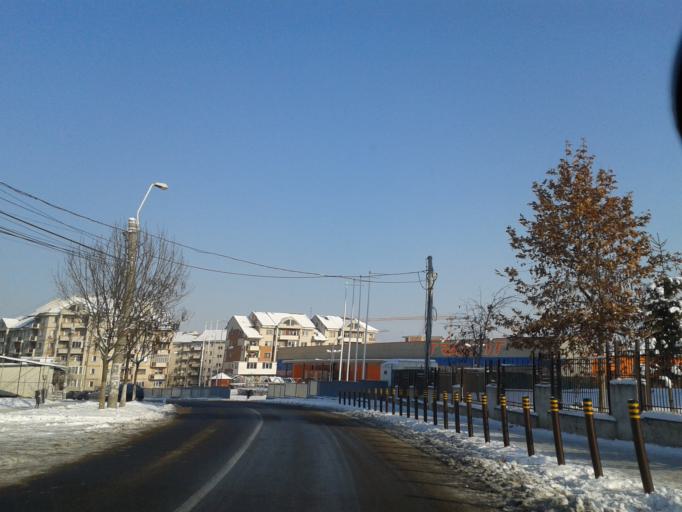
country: RO
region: Hunedoara
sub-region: Municipiul Deva
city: Deva
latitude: 45.8609
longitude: 22.9092
